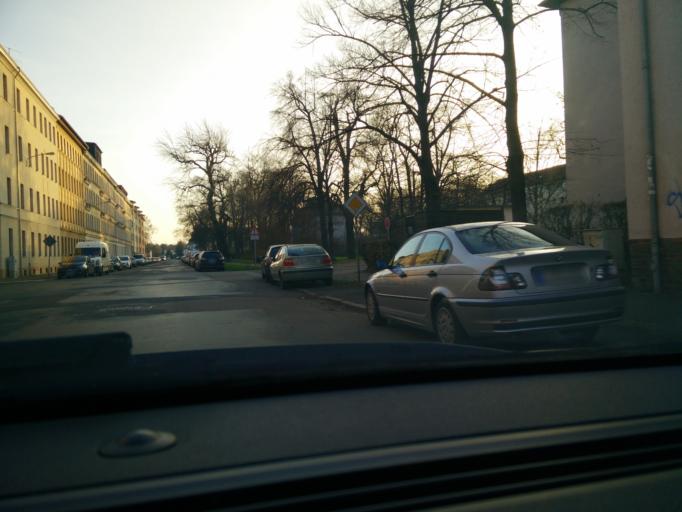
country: DE
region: Saxony
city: Leipzig
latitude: 51.3190
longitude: 12.4263
